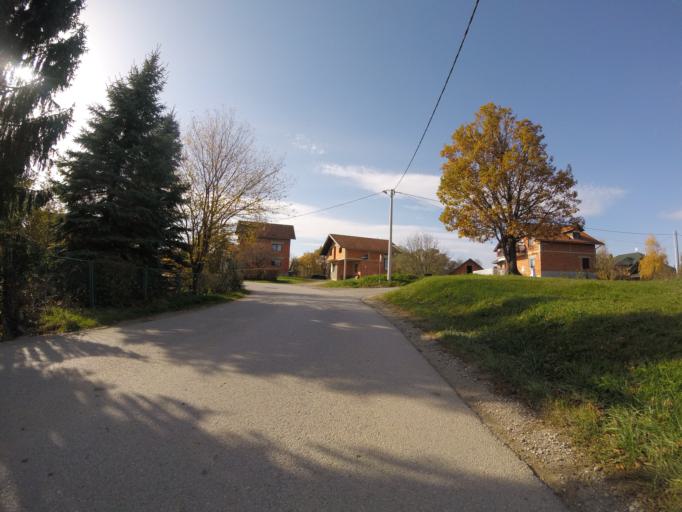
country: HR
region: Zagrebacka
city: Lukavec
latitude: 45.6158
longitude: 16.0098
